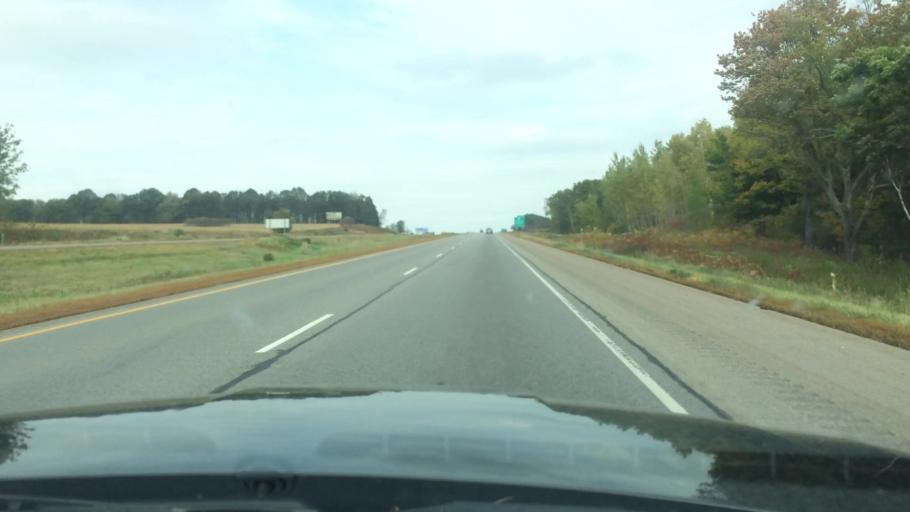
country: US
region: Wisconsin
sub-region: Marathon County
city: Mosinee
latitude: 44.7637
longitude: -89.6799
